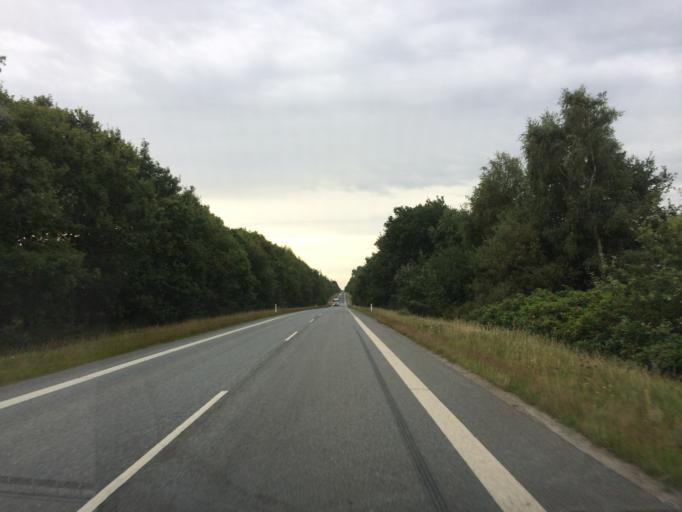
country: DK
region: Central Jutland
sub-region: Ikast-Brande Kommune
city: Brande
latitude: 55.9866
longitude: 9.0525
